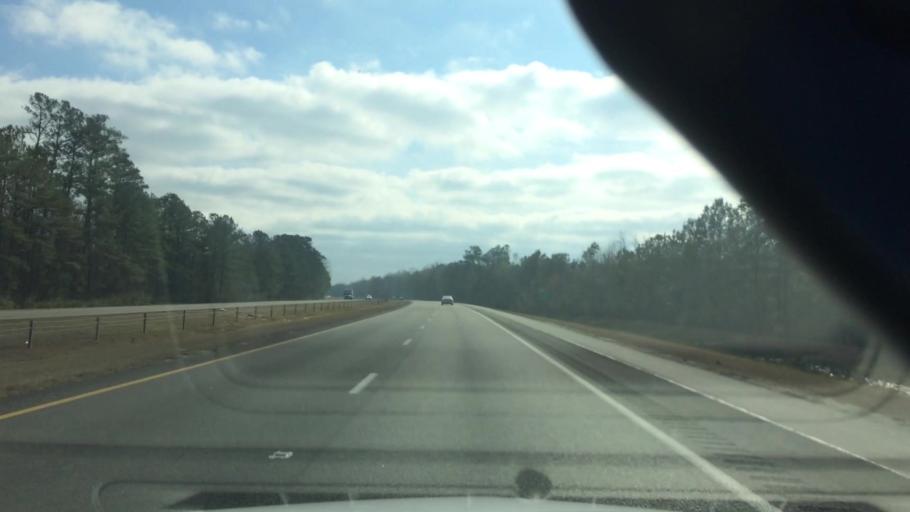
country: US
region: North Carolina
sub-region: Pender County
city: Rocky Point
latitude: 34.4643
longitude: -77.8802
